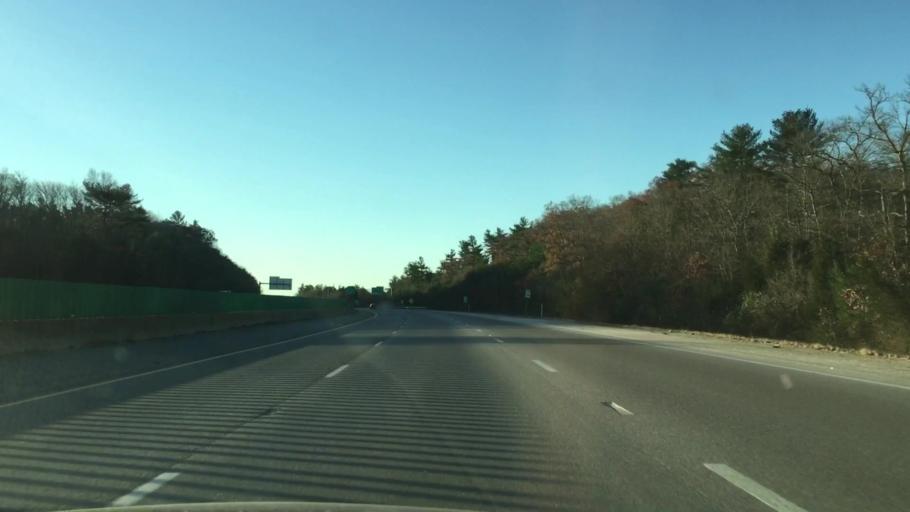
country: US
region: Massachusetts
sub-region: Bristol County
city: Raynham Center
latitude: 41.9641
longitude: -71.0286
